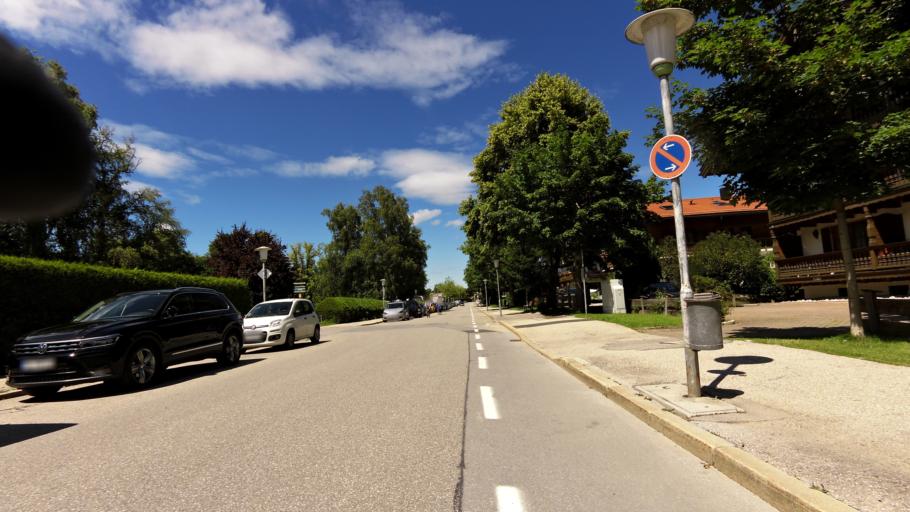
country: DE
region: Bavaria
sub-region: Upper Bavaria
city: Bad Wiessee
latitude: 47.7168
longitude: 11.7248
